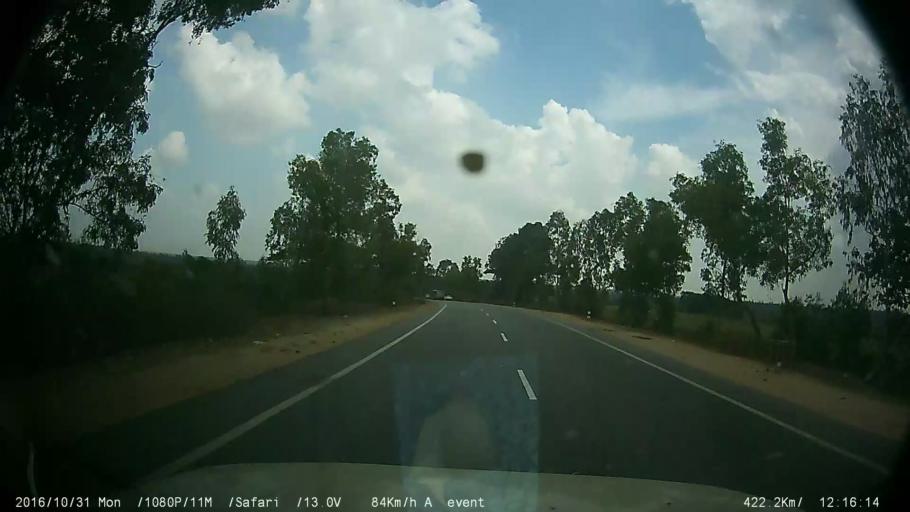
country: IN
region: Karnataka
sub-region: Mysore
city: Hunsur
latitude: 12.3363
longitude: 76.3864
